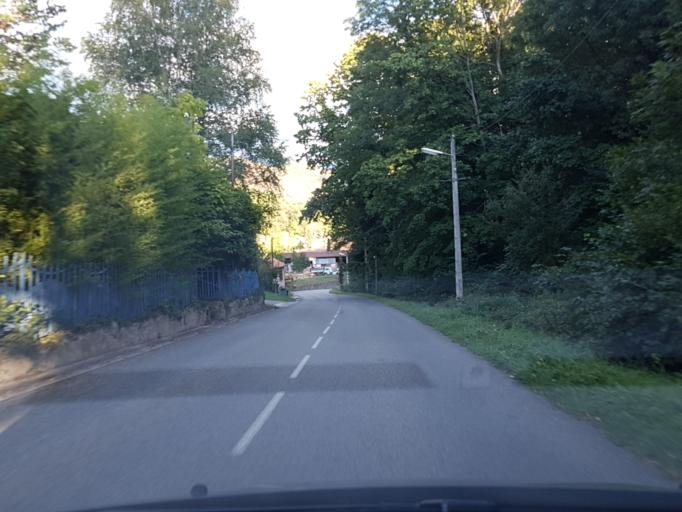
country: FR
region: Midi-Pyrenees
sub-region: Departement de l'Ariege
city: Tarascon-sur-Ariege
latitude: 42.8587
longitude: 1.5786
